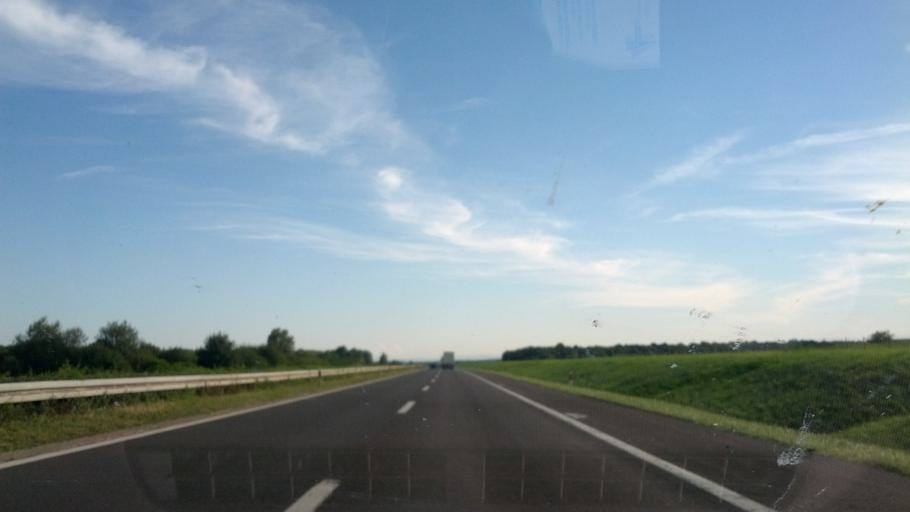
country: HR
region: Zagrebacka
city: Jastrebarsko
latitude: 45.6237
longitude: 15.6527
